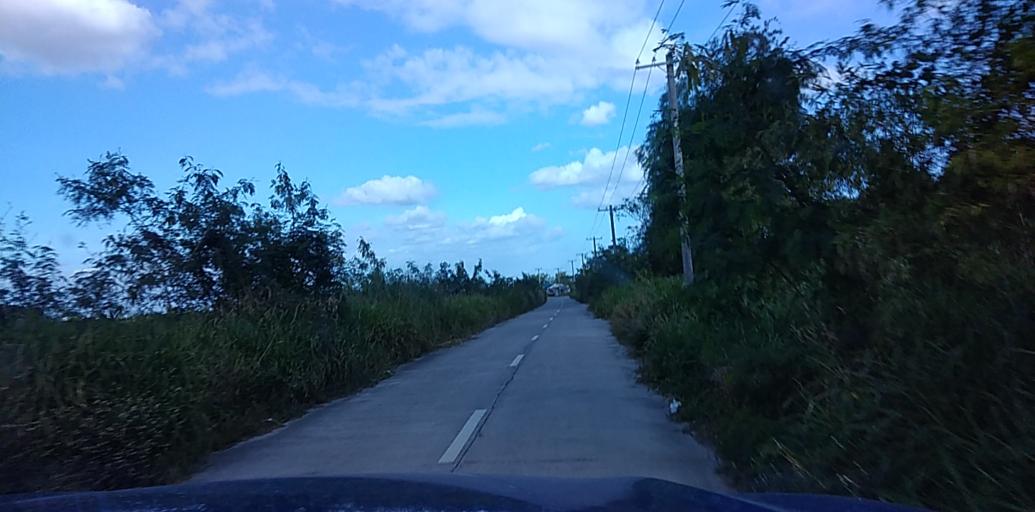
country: PH
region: Central Luzon
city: Santol
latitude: 15.1476
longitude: 120.5349
